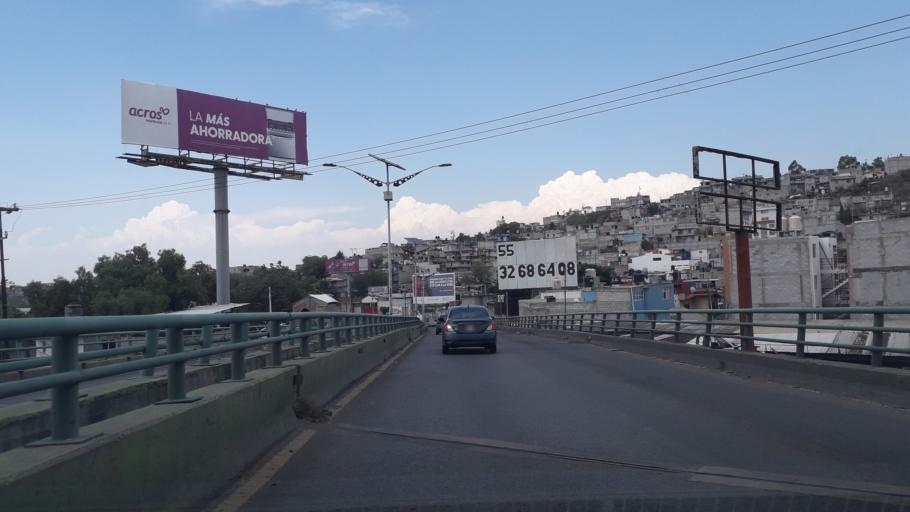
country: MX
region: Mexico
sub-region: Tultitlan
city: Buenavista
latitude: 19.6067
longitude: -99.1822
